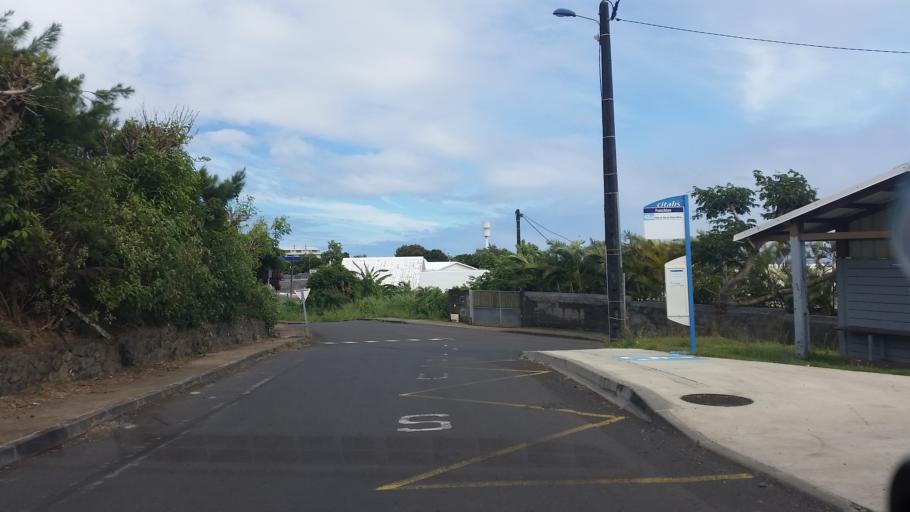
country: RE
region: Reunion
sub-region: Reunion
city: Sainte-Marie
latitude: -20.9177
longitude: 55.5313
